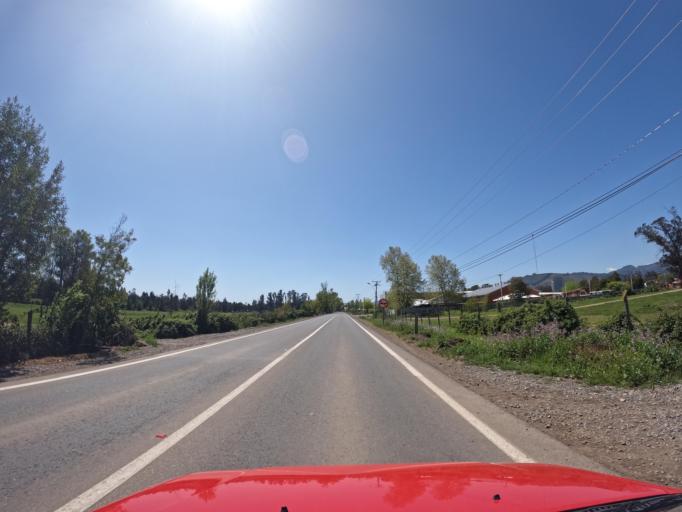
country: CL
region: Maule
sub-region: Provincia de Linares
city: Colbun
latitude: -35.7592
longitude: -71.4196
